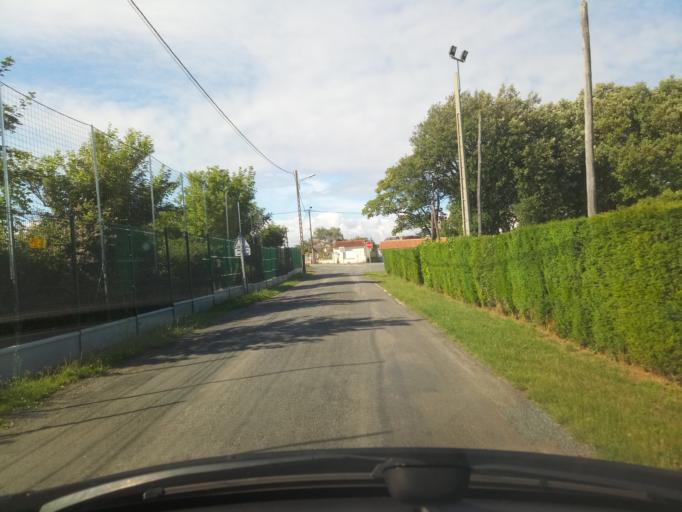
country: FR
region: Poitou-Charentes
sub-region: Departement de la Charente-Maritime
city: Marans
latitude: 46.3029
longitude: -0.9941
